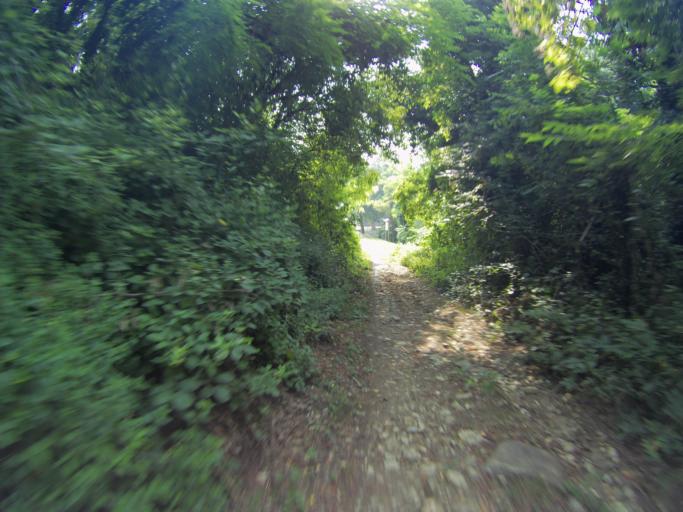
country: IT
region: Emilia-Romagna
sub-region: Provincia di Reggio Emilia
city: Pratissolo
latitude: 44.5868
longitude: 10.6607
